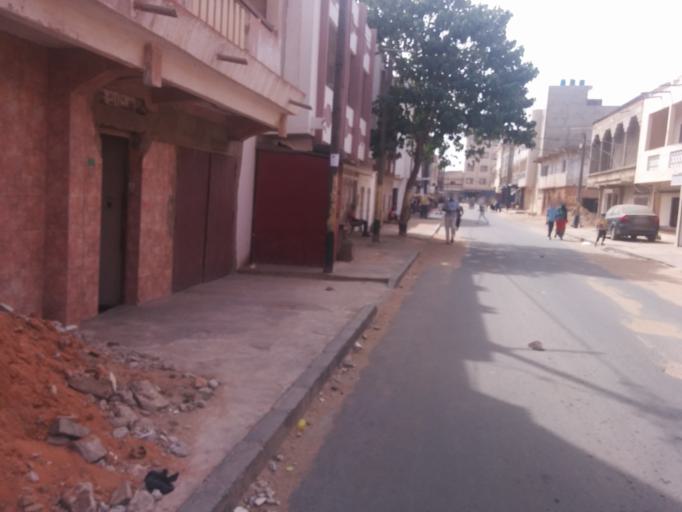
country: SN
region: Dakar
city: Pikine
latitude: 14.7632
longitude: -17.4359
